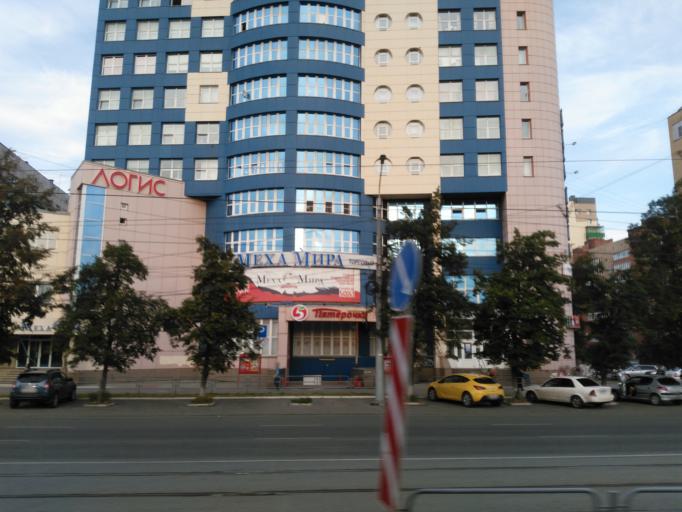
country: RU
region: Chelyabinsk
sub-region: Gorod Chelyabinsk
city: Chelyabinsk
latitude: 55.1748
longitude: 61.3996
